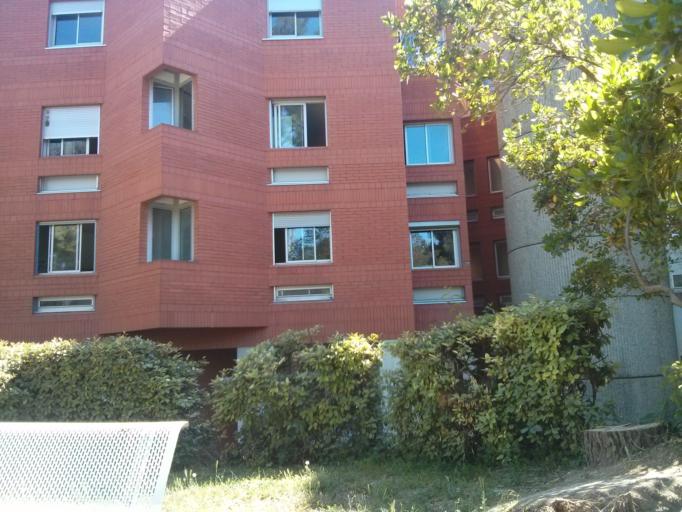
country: FR
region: Languedoc-Roussillon
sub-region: Departement du Gard
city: Nimes
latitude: 43.8237
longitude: 4.3205
